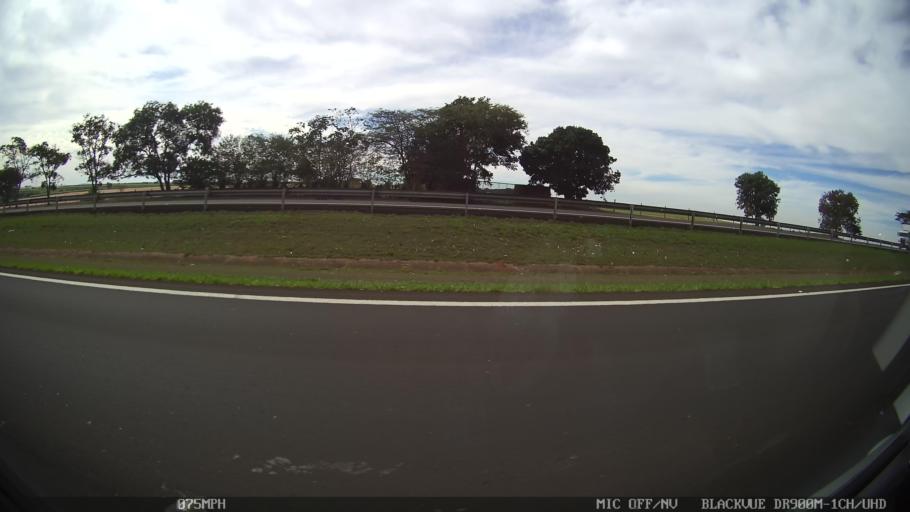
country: BR
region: Sao Paulo
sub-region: Taquaritinga
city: Taquaritinga
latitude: -21.5113
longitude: -48.5470
